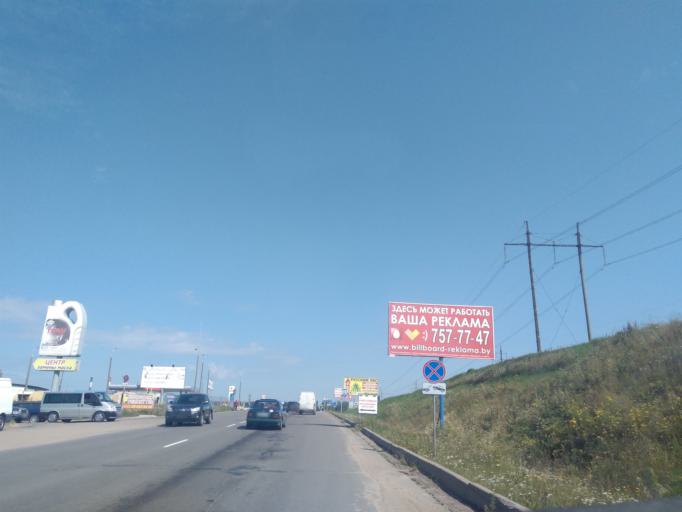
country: BY
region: Minsk
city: Malinovka
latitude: 53.8516
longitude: 27.4285
